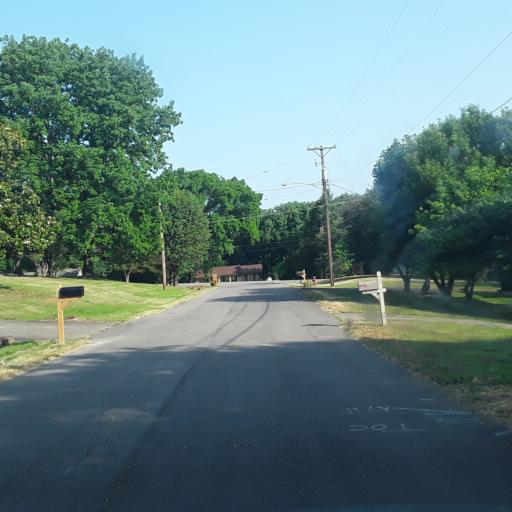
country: US
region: Tennessee
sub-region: Williamson County
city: Brentwood Estates
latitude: 36.0292
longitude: -86.7141
